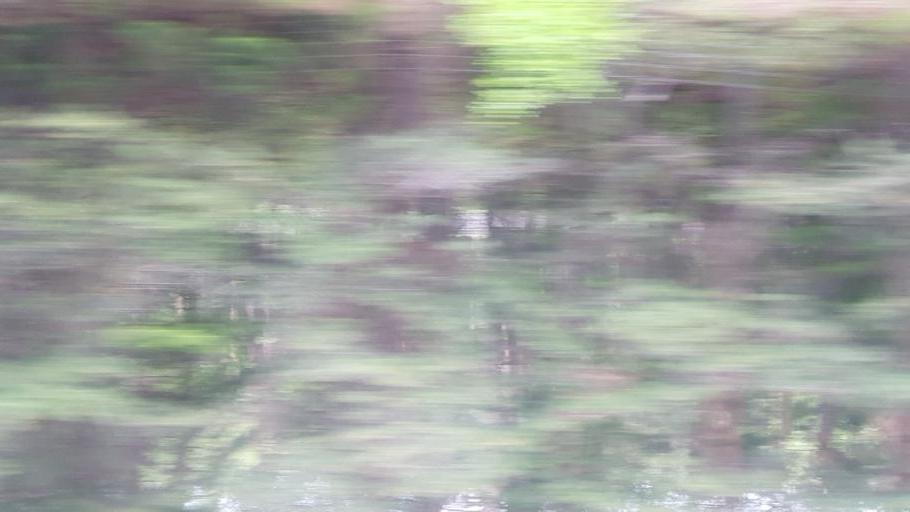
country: NO
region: Oppland
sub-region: Ringebu
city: Ringebu
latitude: 61.5503
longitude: 10.0731
